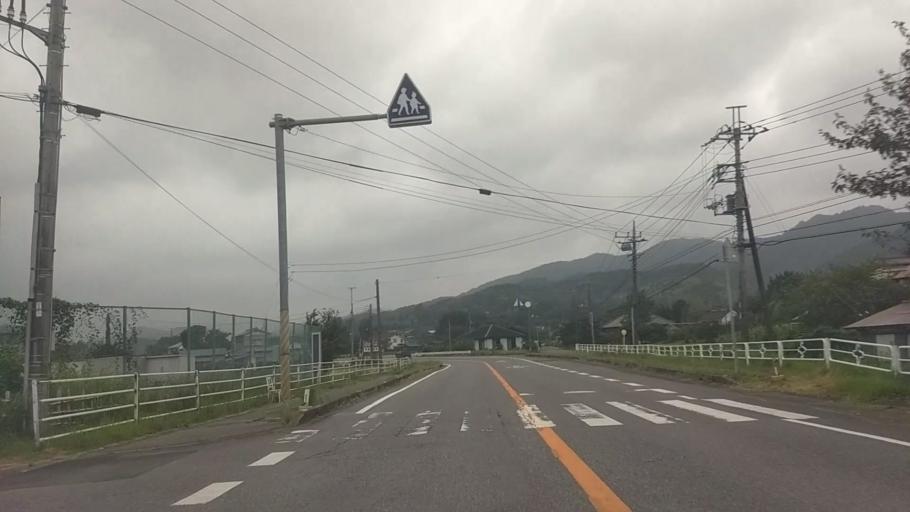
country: JP
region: Chiba
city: Kawaguchi
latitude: 35.1373
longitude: 139.9898
